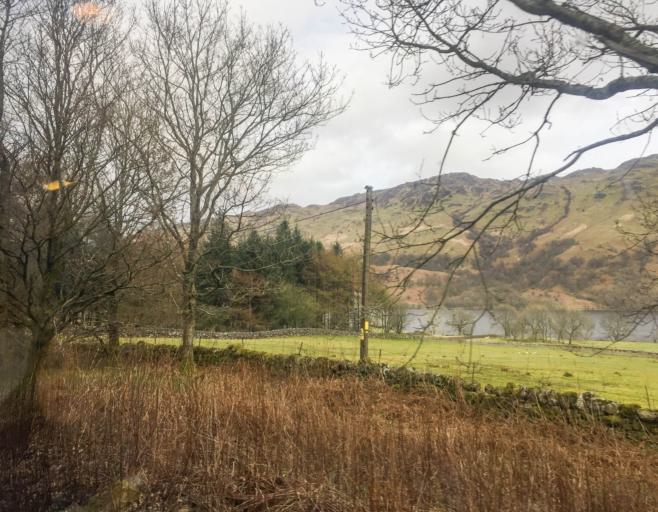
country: GB
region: Scotland
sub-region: Argyll and Bute
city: Garelochhead
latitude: 56.2946
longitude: -4.7144
